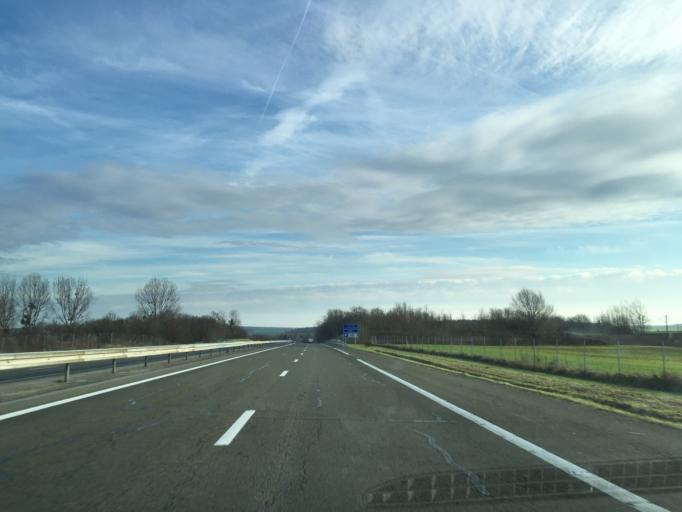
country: FR
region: Picardie
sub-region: Departement de l'Aisne
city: Charly-sur-Marne
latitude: 49.0466
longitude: 3.2745
